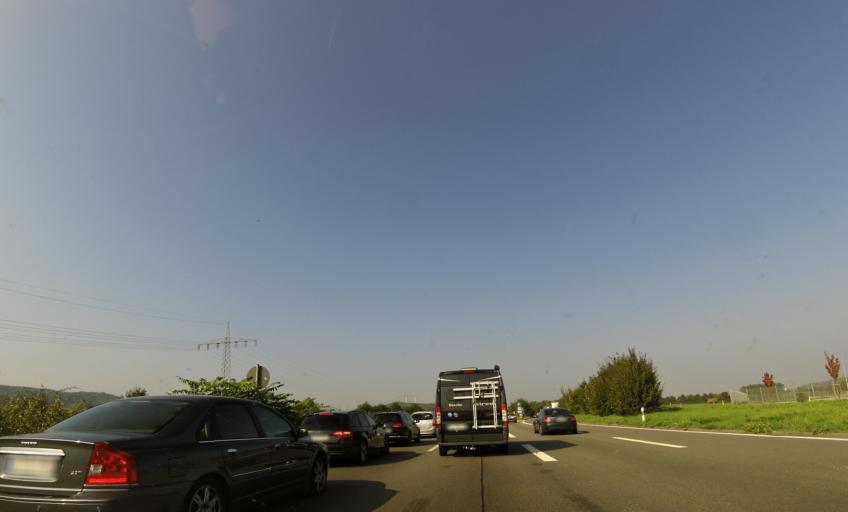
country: DE
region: Baden-Wuerttemberg
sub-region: Regierungsbezirk Stuttgart
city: Erlenbach
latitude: 49.1671
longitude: 9.2613
